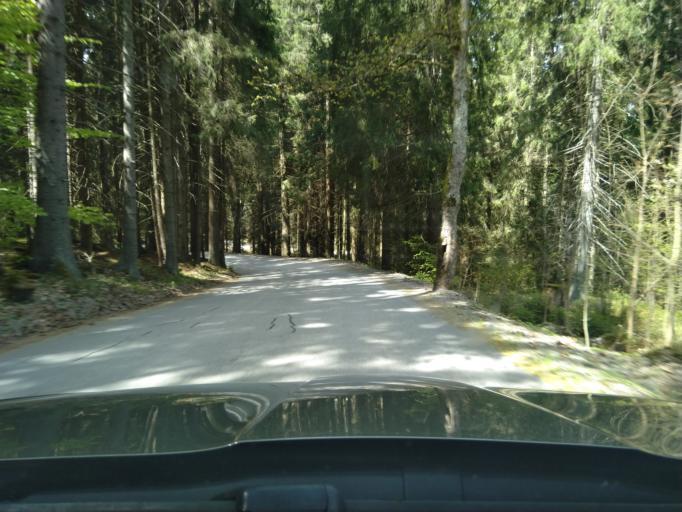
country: CZ
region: Jihocesky
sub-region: Okres Prachatice
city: Vimperk
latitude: 49.0156
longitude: 13.7273
